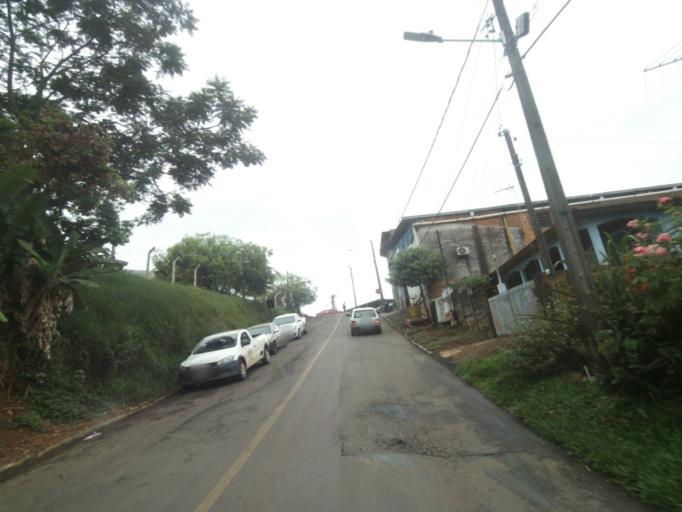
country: BR
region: Parana
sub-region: Telemaco Borba
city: Telemaco Borba
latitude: -24.3296
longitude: -50.6454
